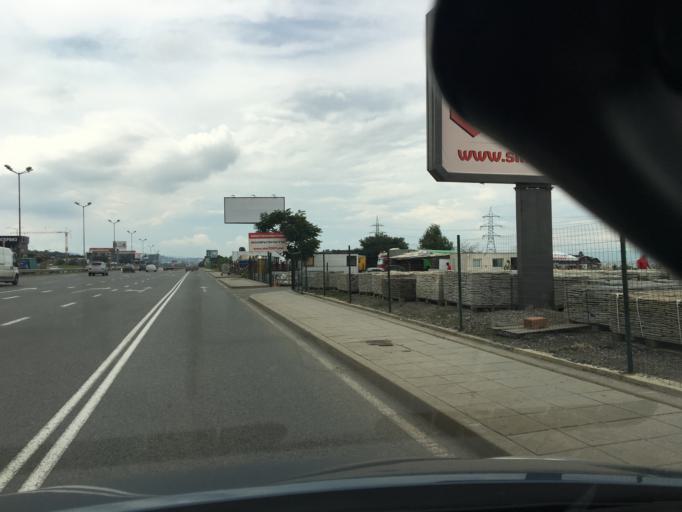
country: BG
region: Sofia-Capital
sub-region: Stolichna Obshtina
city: Sofia
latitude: 42.6398
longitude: 23.3175
